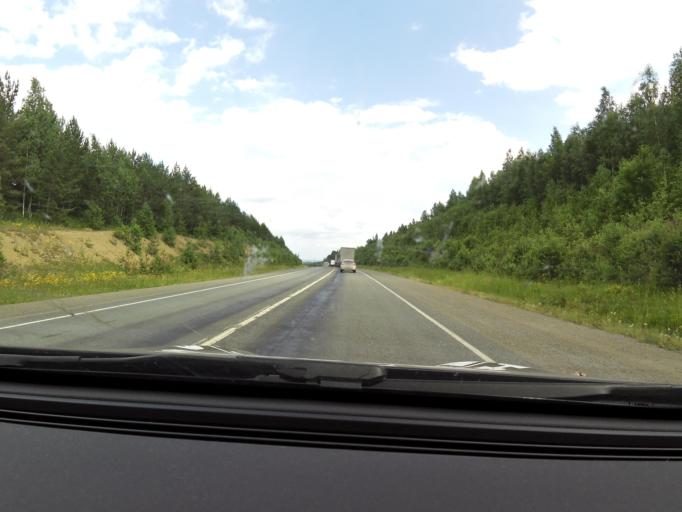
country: RU
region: Sverdlovsk
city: Bisert'
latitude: 56.8270
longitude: 58.9955
